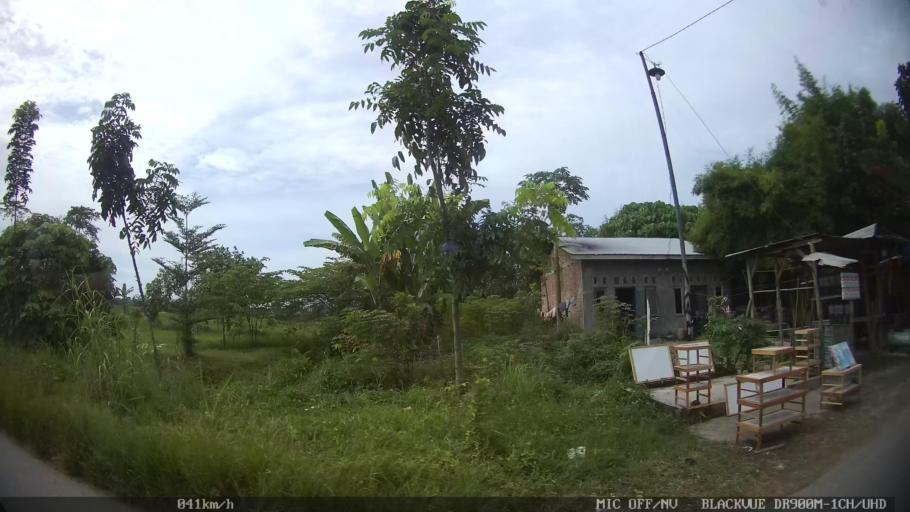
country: ID
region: North Sumatra
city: Percut
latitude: 3.6200
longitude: 98.7684
